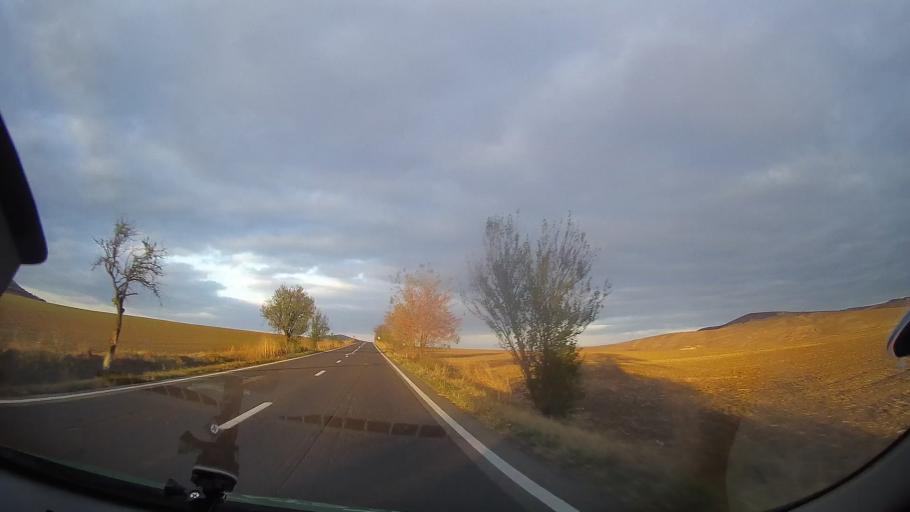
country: RO
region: Tulcea
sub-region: Comuna Nalbant
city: Nicolae Balcescu
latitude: 44.9776
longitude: 28.5463
